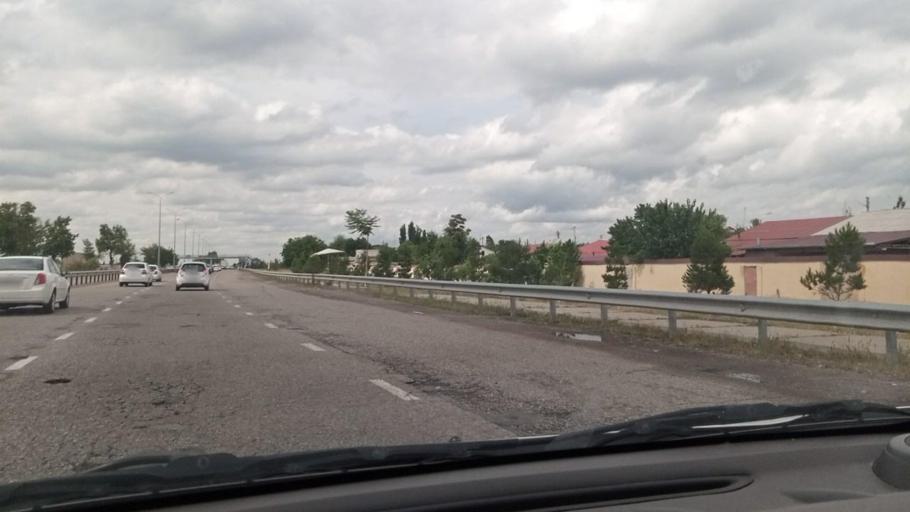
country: UZ
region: Toshkent
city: Tuytepa
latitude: 41.1267
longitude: 69.4377
